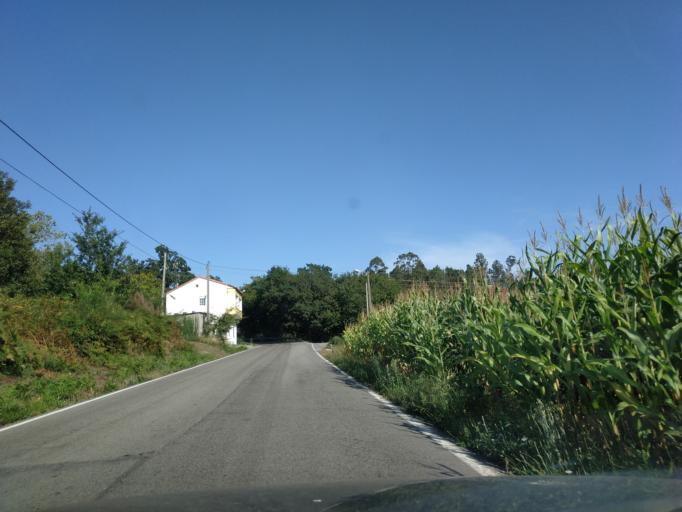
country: ES
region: Galicia
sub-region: Provincia da Coruna
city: Cerceda
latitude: 43.2329
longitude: -8.4769
